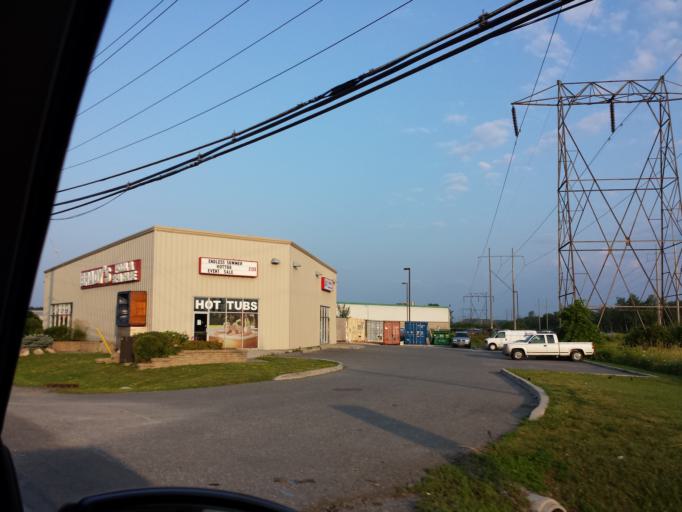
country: CA
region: Ontario
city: Bells Corners
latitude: 45.3203
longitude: -75.8378
